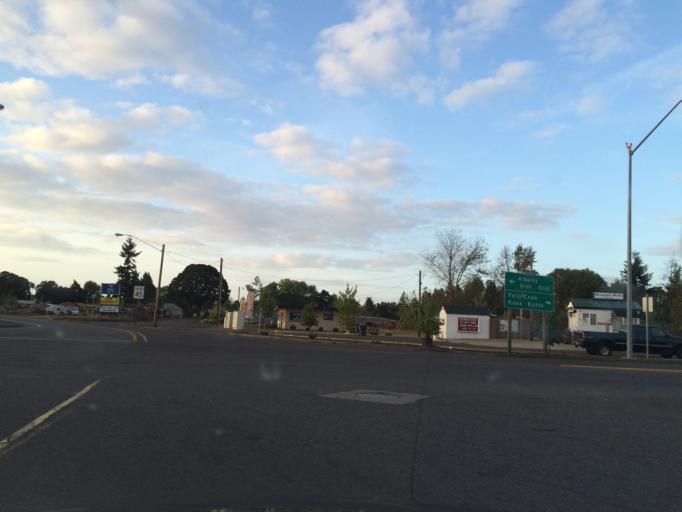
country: US
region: Oregon
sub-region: Linn County
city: Millersburg
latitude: 44.6443
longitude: -123.0594
